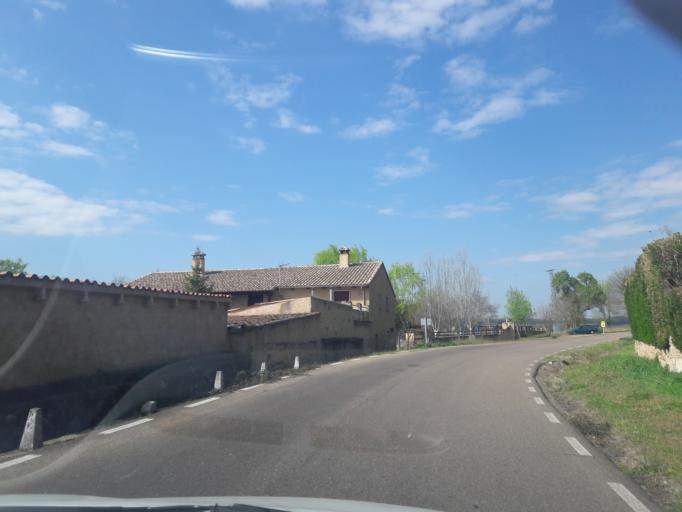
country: ES
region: Castille and Leon
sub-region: Provincia de Salamanca
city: Zamarra
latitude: 40.5672
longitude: -6.4773
